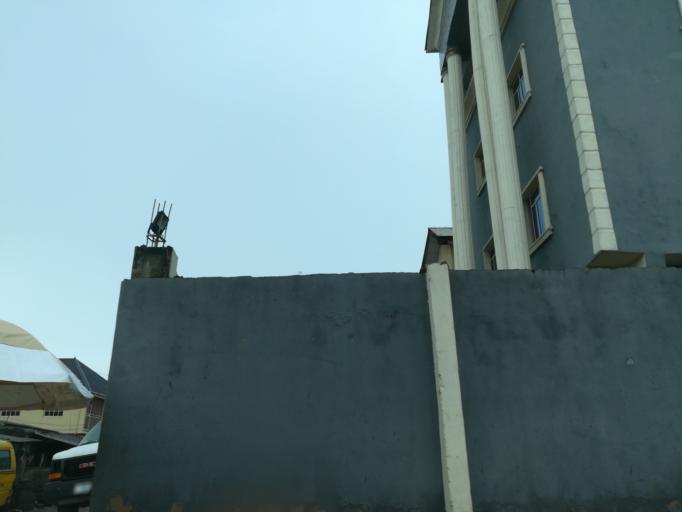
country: NG
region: Lagos
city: Oshodi
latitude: 6.5602
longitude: 3.3376
